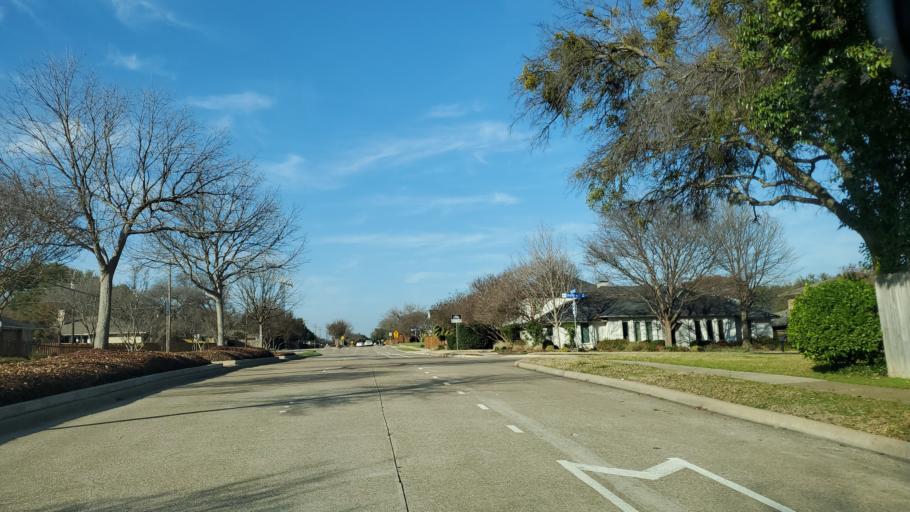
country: US
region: Texas
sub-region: Collin County
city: Plano
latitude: 32.9930
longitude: -96.7168
